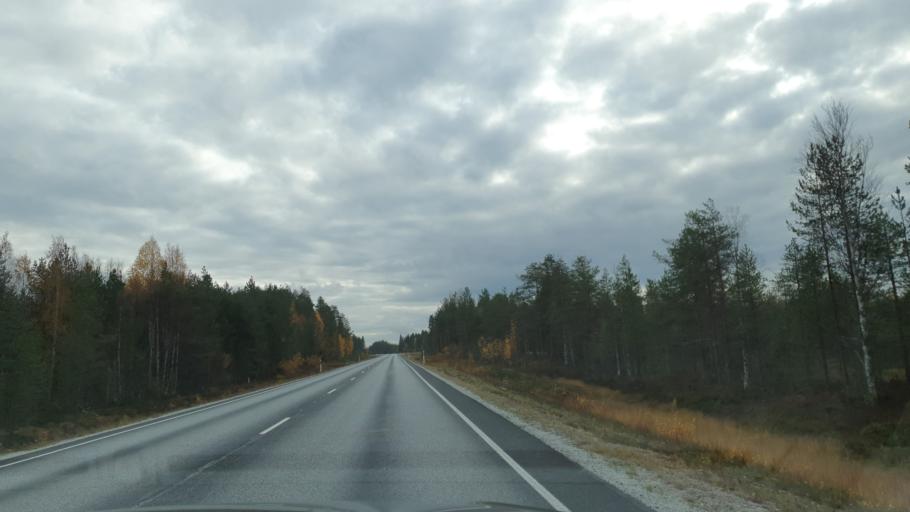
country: FI
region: Northern Ostrobothnia
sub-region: Oulunkaari
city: Pudasjaervi
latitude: 65.4203
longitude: 26.8736
